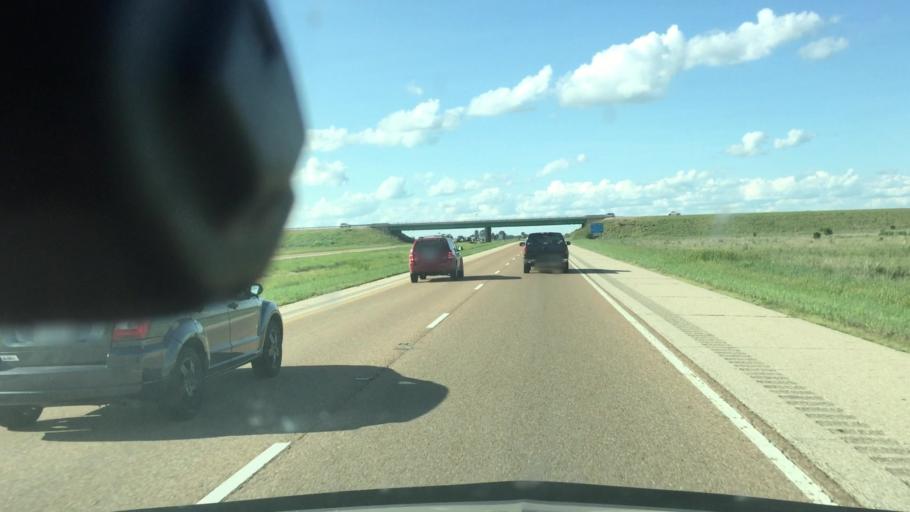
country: US
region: Illinois
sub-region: Montgomery County
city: Raymond
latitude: 39.3193
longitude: -89.6425
